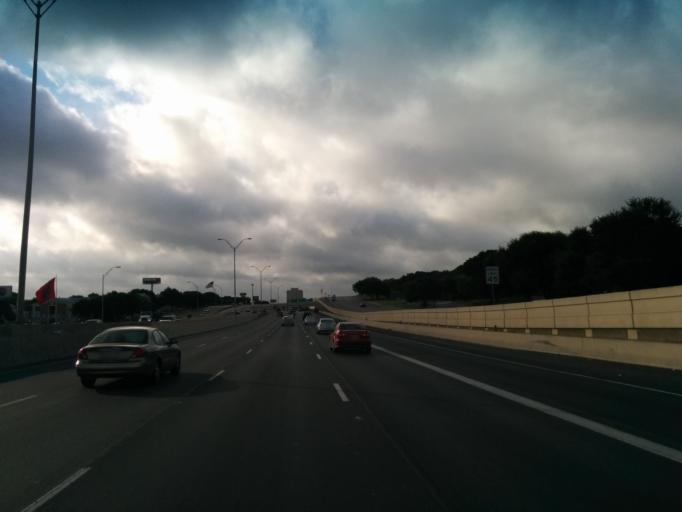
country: US
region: Texas
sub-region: Bexar County
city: Shavano Park
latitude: 29.5425
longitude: -98.5757
